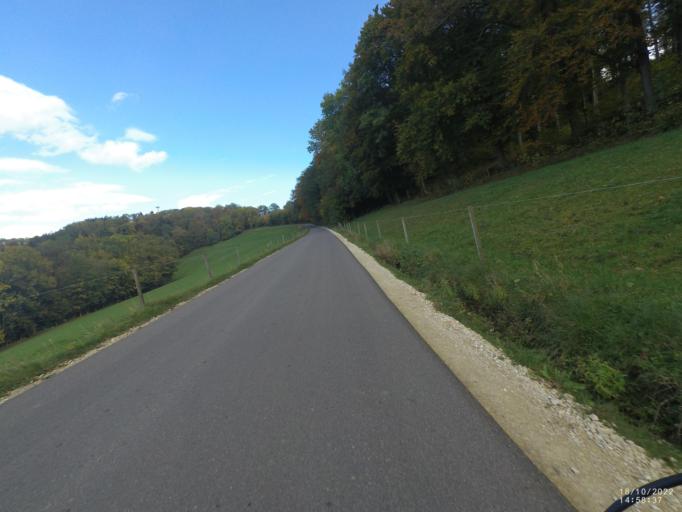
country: DE
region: Baden-Wuerttemberg
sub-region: Regierungsbezirk Stuttgart
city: Ottenbach
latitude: 48.7339
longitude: 9.7766
